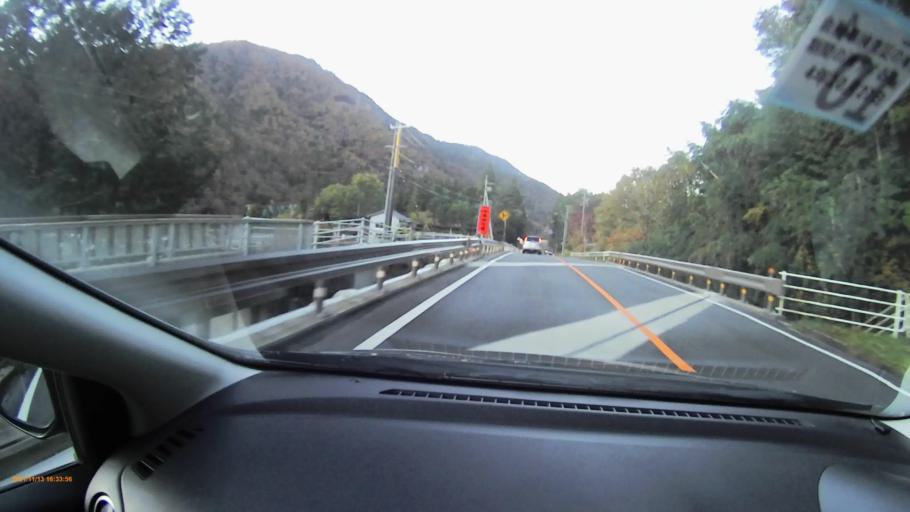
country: JP
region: Gifu
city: Nakatsugawa
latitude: 35.5887
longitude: 137.5978
